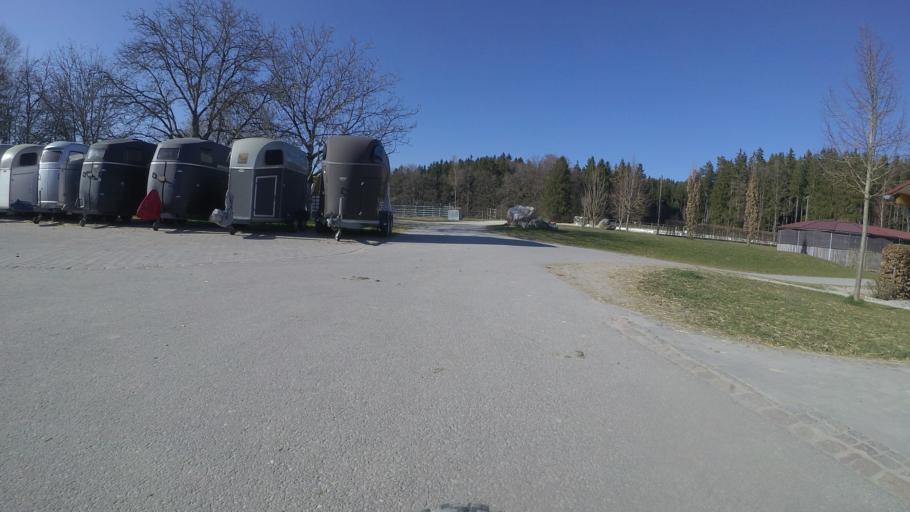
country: DE
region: Bavaria
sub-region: Upper Bavaria
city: Chieming
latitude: 47.9312
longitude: 12.5429
